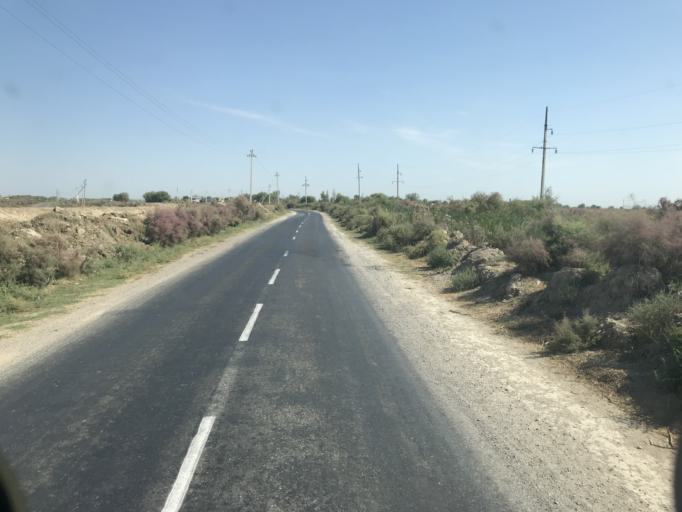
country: KZ
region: Ongtustik Qazaqstan
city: Myrzakent
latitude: 40.7263
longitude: 68.5354
